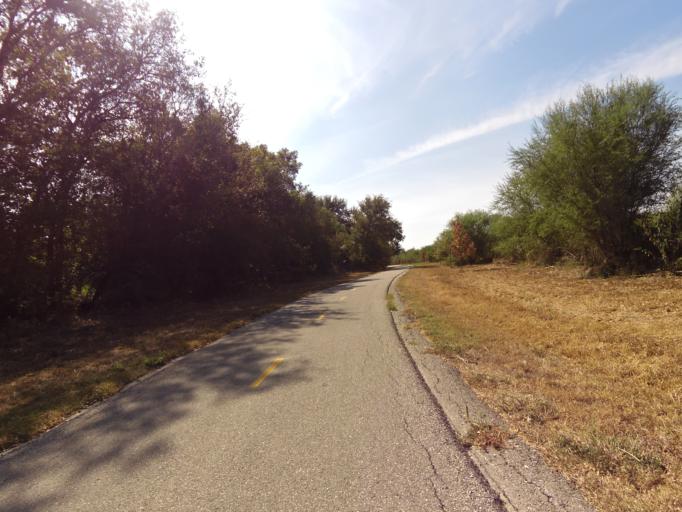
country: US
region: Texas
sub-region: Bexar County
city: Kirby
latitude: 29.4381
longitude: -98.4198
